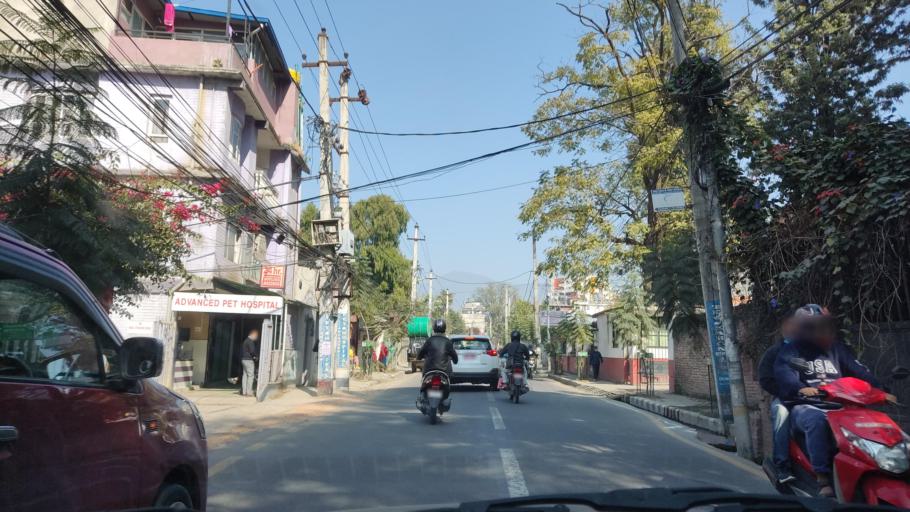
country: NP
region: Central Region
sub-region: Bagmati Zone
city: Kathmandu
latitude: 27.7201
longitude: 85.3345
